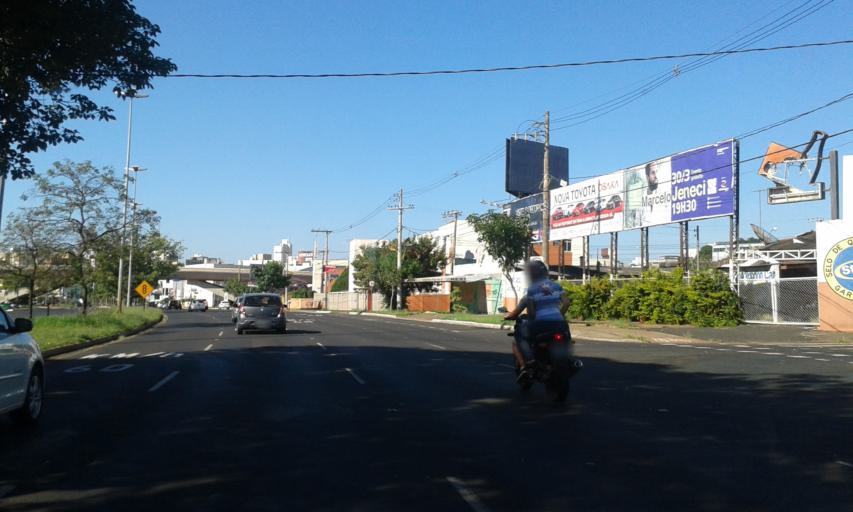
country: BR
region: Minas Gerais
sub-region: Uberlandia
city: Uberlandia
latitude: -18.9095
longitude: -48.2623
